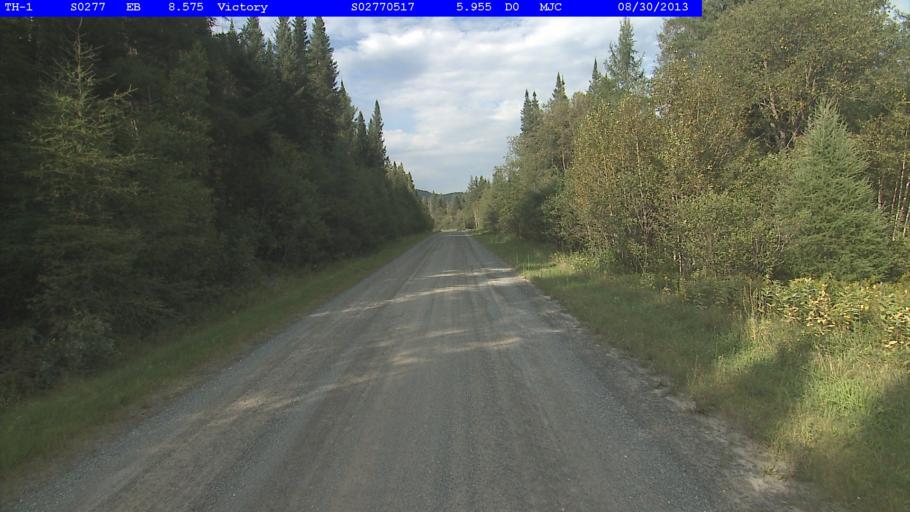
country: US
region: Vermont
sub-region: Caledonia County
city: Lyndonville
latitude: 44.5541
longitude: -71.7870
